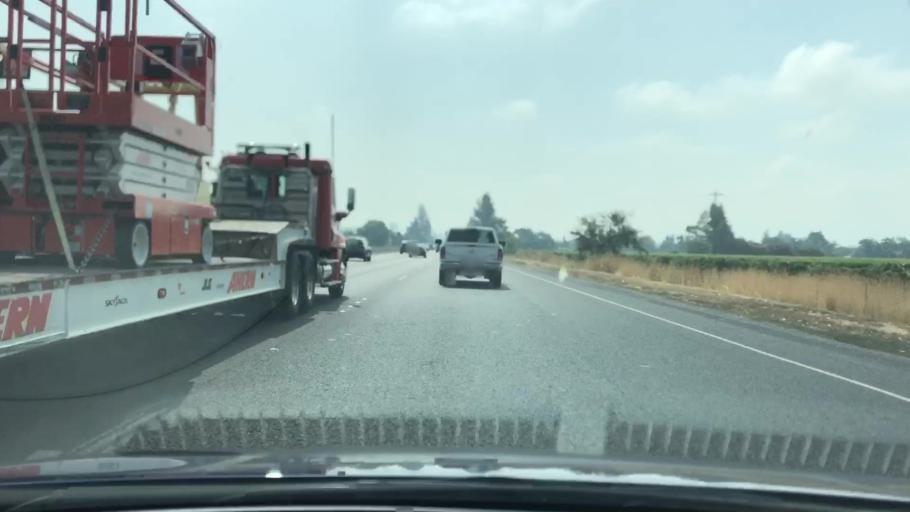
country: US
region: California
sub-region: Sonoma County
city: Larkfield-Wikiup
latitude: 38.4939
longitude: -122.7533
